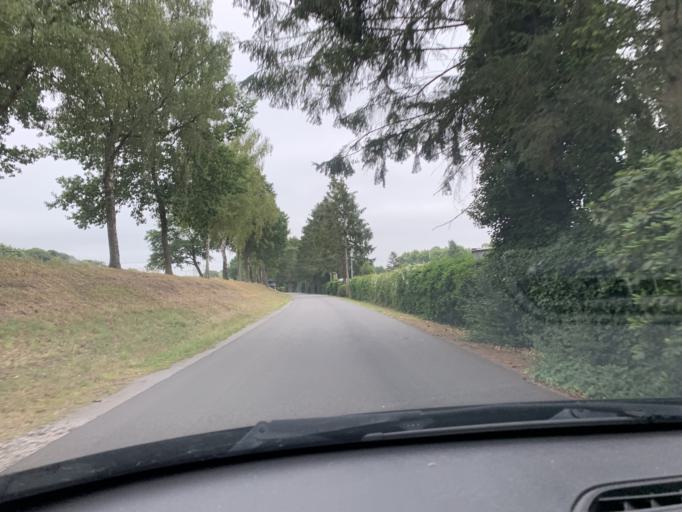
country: DE
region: Lower Saxony
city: Lingen
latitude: 52.4731
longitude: 7.3030
